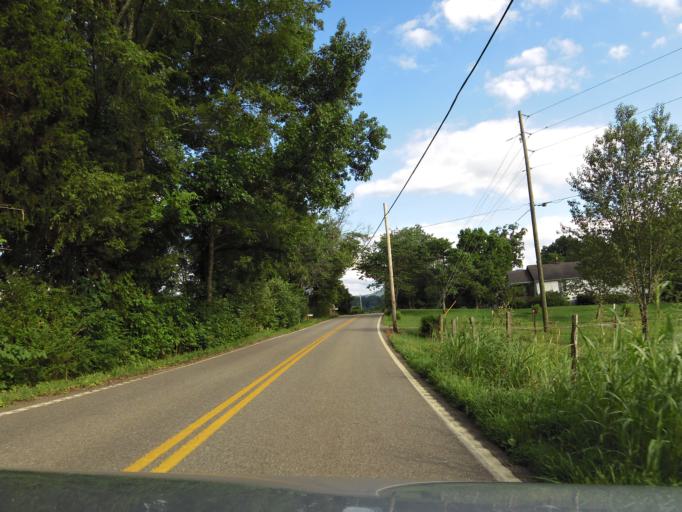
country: US
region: Tennessee
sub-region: Loudon County
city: Greenback
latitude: 35.6223
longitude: -84.0952
